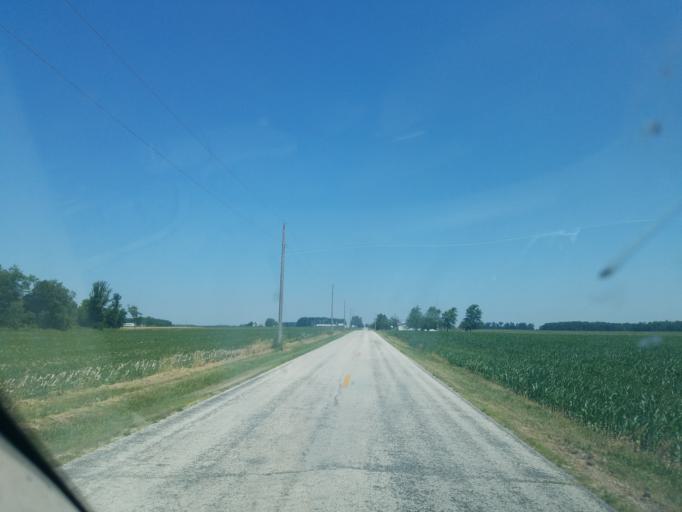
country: US
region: Ohio
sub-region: Mercer County
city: Rockford
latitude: 40.5866
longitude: -84.7084
